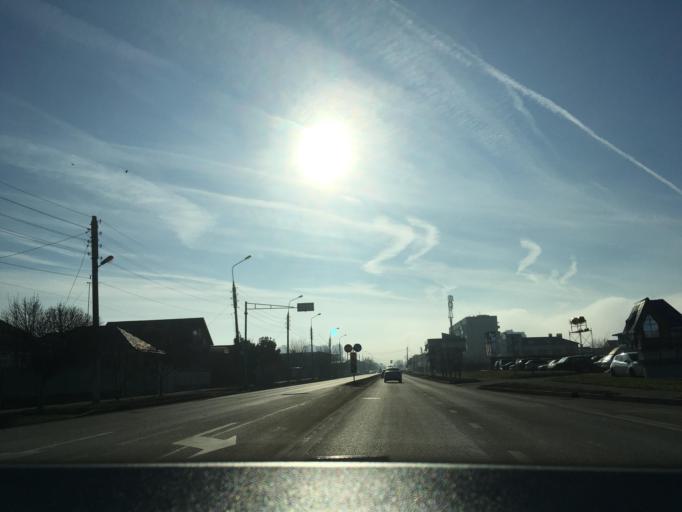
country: RU
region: Krasnodarskiy
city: Krasnodar
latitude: 45.1182
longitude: 39.0115
